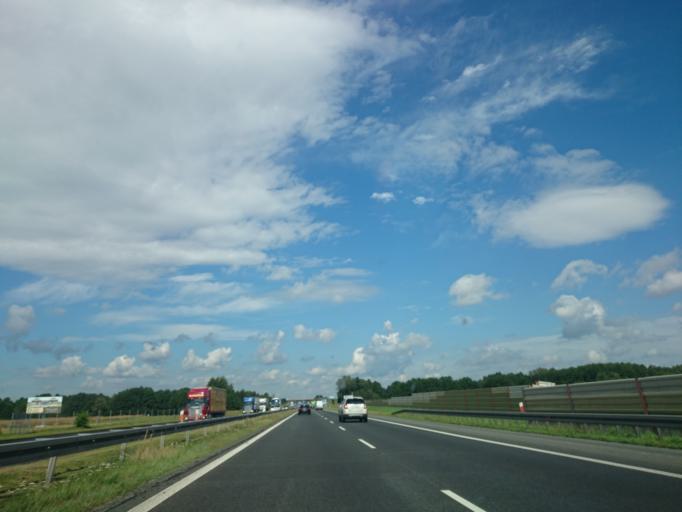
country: PL
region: Opole Voivodeship
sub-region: Powiat opolski
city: Proszkow
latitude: 50.5614
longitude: 17.8742
